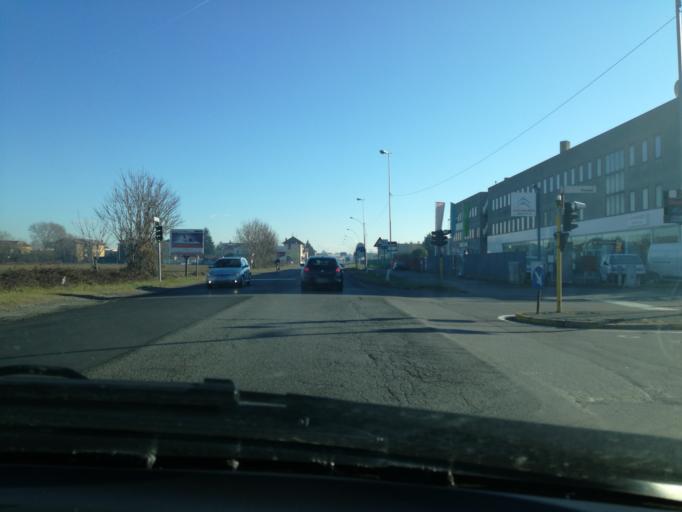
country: IT
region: Lombardy
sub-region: Provincia di Monza e Brianza
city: Concorezzo
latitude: 45.5805
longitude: 9.3165
